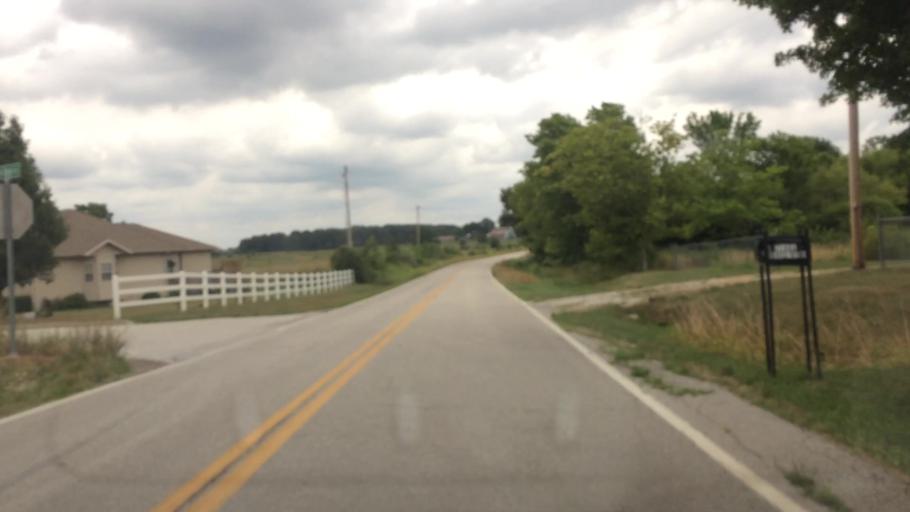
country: US
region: Missouri
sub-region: Greene County
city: Strafford
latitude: 37.2824
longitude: -93.1105
